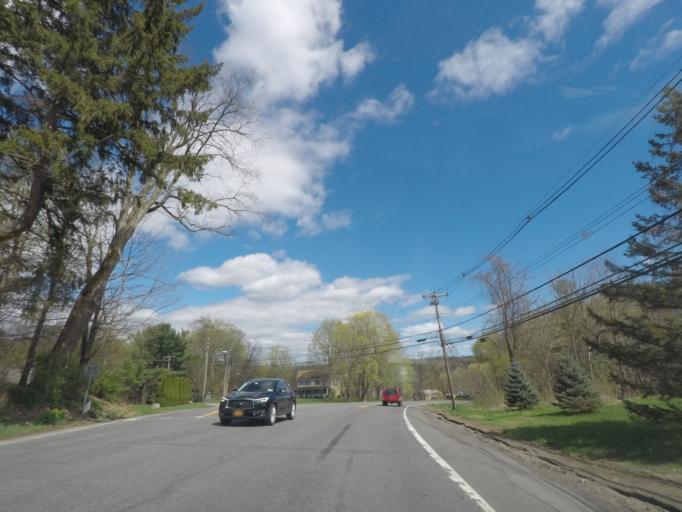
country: US
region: New York
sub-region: Columbia County
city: Lorenz Park
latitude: 42.2247
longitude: -73.7183
